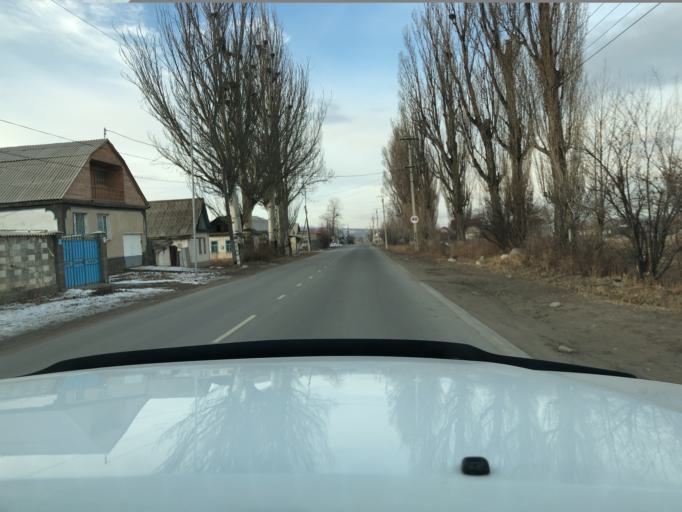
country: KG
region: Ysyk-Koel
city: Karakol
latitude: 42.4687
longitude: 78.3758
